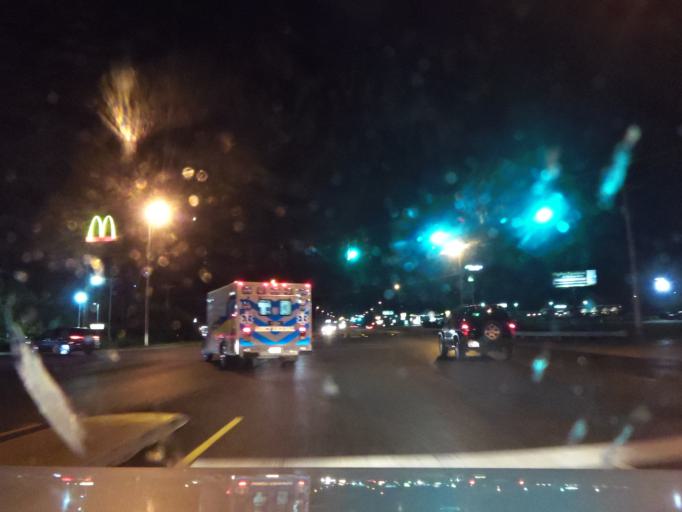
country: US
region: Kentucky
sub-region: McCracken County
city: Hendron
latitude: 37.0793
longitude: -88.6779
